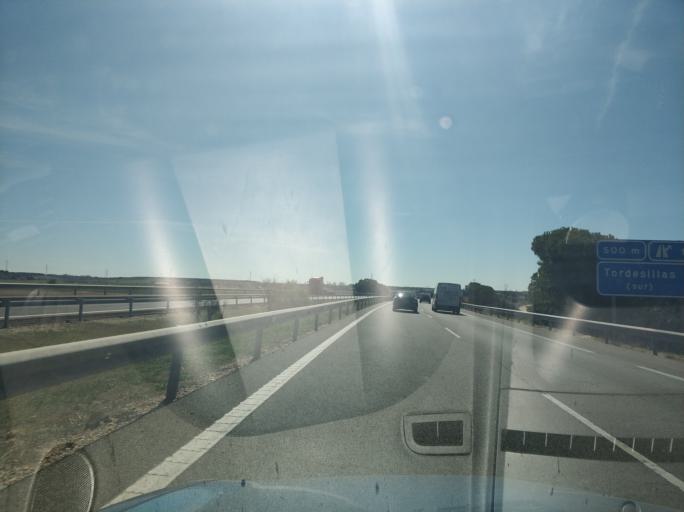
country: ES
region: Castille and Leon
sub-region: Provincia de Valladolid
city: Tordesillas
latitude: 41.4882
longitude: -4.9851
